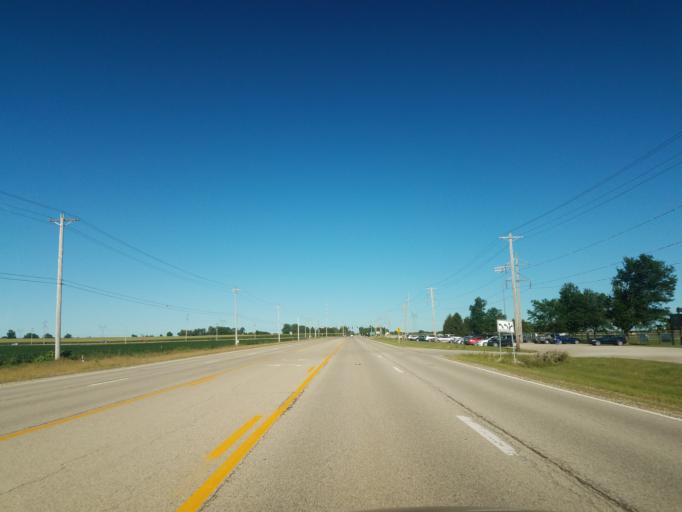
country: US
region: Illinois
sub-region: McLean County
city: Downs
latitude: 40.4583
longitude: -88.9061
